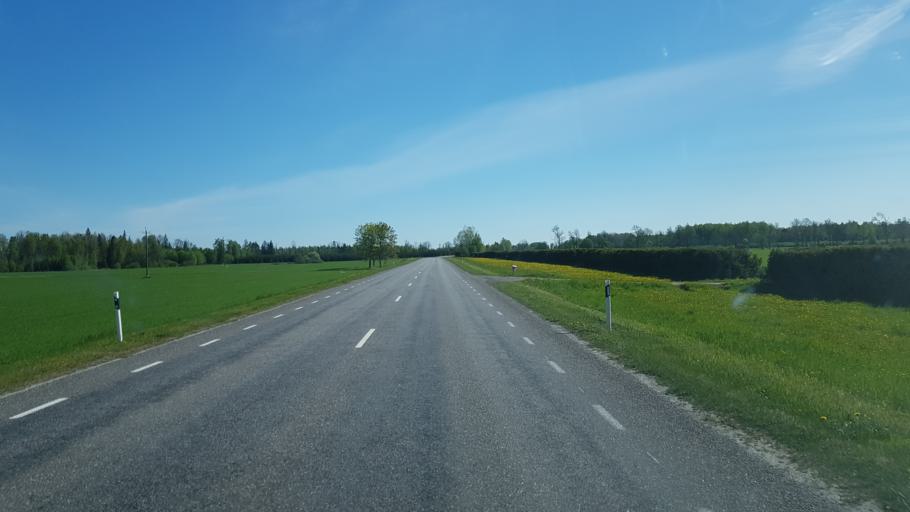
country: EE
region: Jogevamaa
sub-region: Poltsamaa linn
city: Poltsamaa
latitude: 58.6972
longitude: 26.1393
